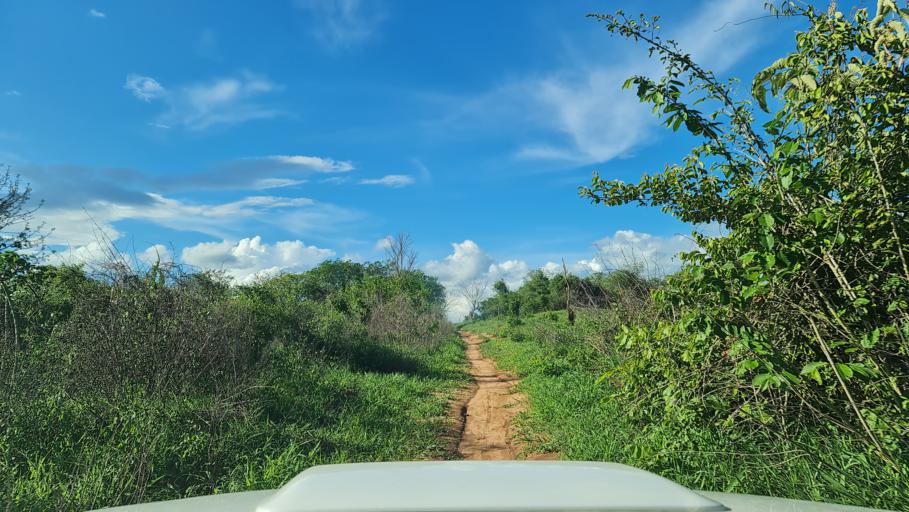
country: MZ
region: Nampula
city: Ilha de Mocambique
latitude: -15.2522
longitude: 40.1813
